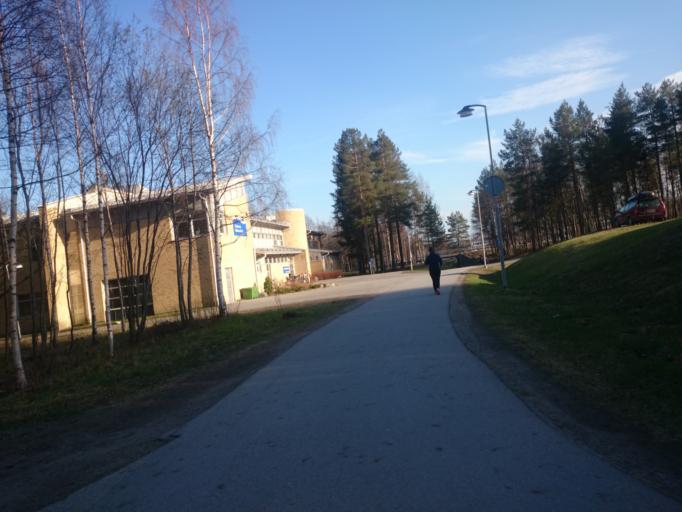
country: SE
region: Vaesterbotten
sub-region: Umea Kommun
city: Umea
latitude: 63.8155
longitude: 20.3162
